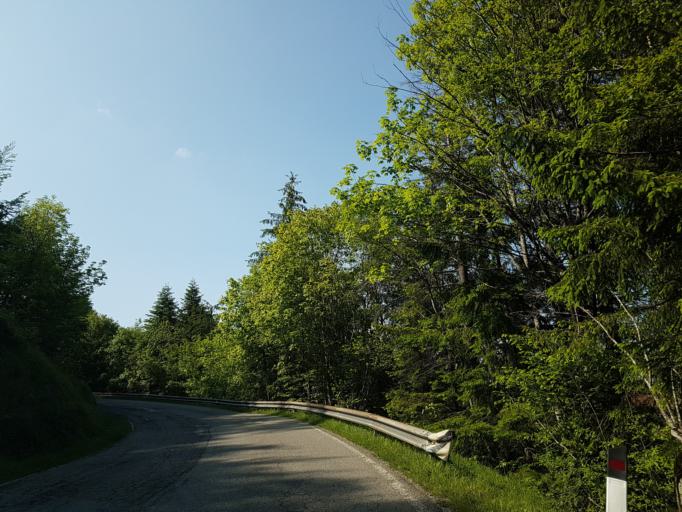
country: IT
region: Emilia-Romagna
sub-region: Forli-Cesena
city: San Piero in Bagno
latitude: 43.8144
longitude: 11.9166
